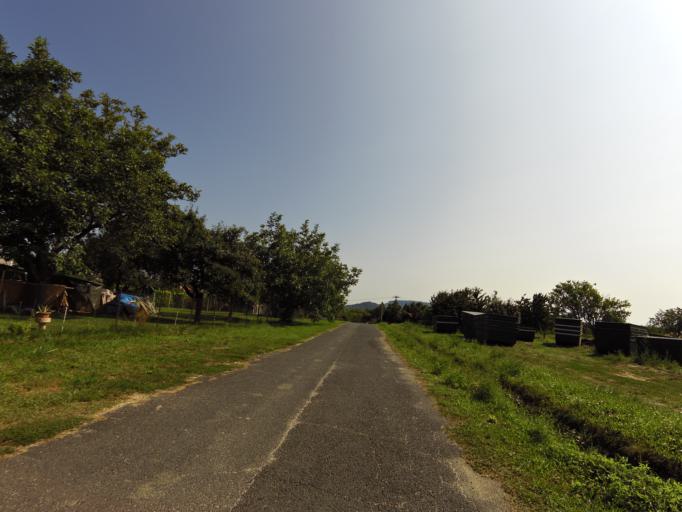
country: HU
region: Zala
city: Vonyarcvashegy
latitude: 46.7978
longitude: 17.3816
